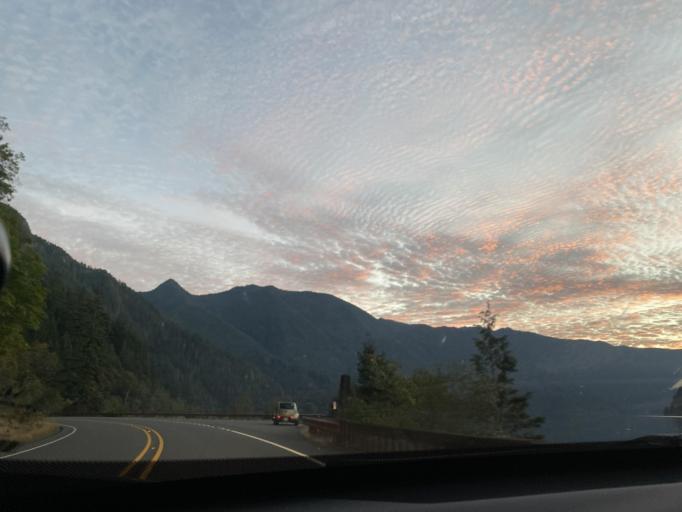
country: CA
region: British Columbia
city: Sooke
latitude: 48.0725
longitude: -123.7737
